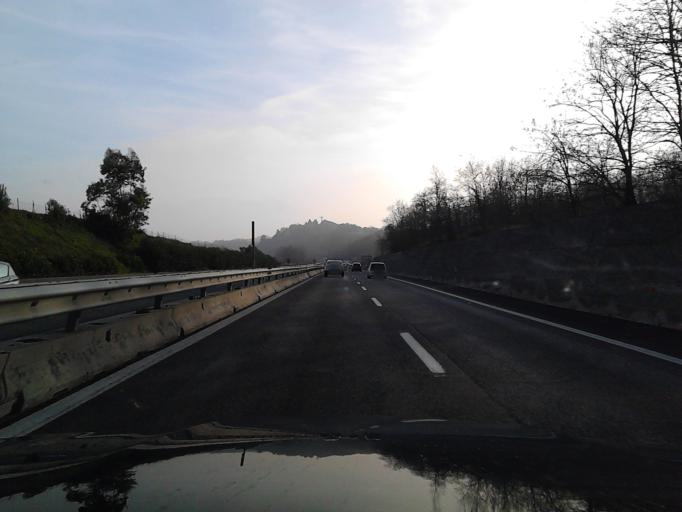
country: IT
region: Abruzzo
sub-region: Provincia di Pescara
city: Spoltore
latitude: 42.4516
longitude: 14.1181
